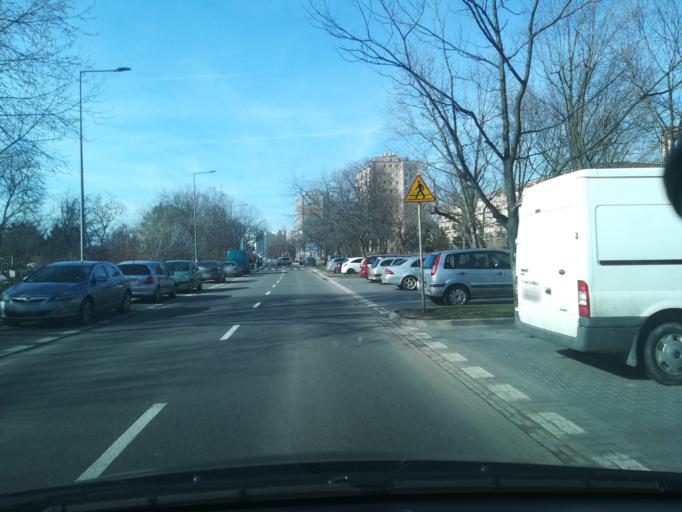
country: PL
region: Masovian Voivodeship
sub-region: Warszawa
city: Praga Poludnie
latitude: 52.2379
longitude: 21.0755
